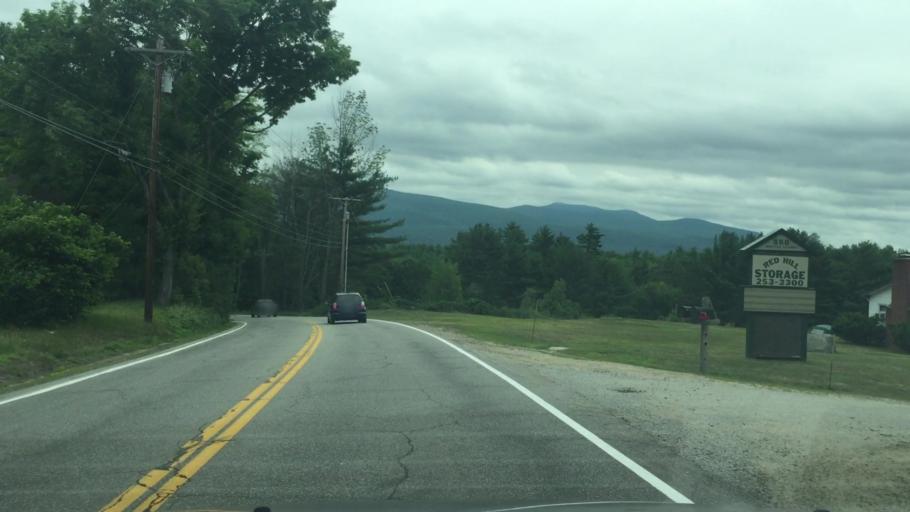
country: US
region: New Hampshire
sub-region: Carroll County
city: Moultonborough
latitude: 43.7300
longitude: -71.4211
